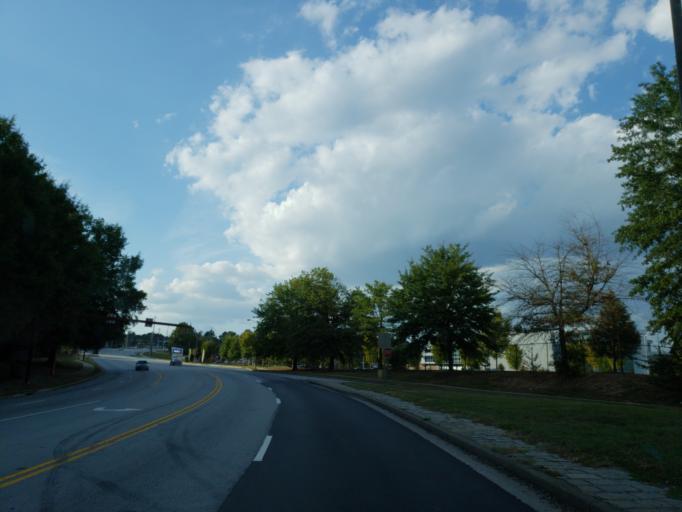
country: US
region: Georgia
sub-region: Cobb County
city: Mableton
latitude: 33.7699
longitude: -84.5575
